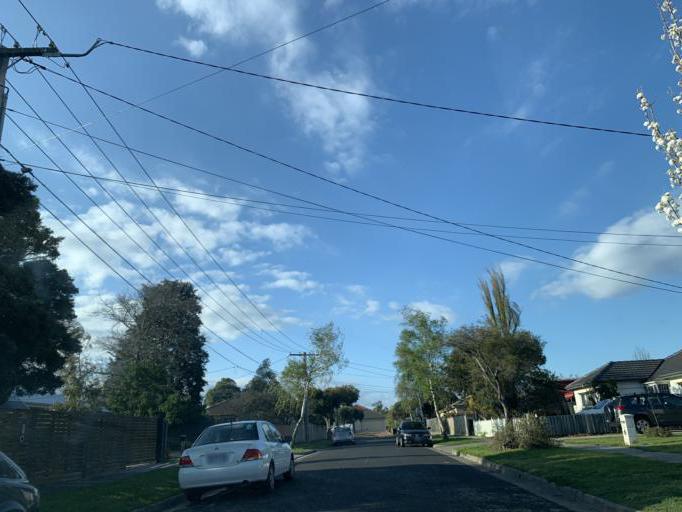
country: AU
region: Victoria
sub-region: Kingston
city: Mordialloc
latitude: -37.9884
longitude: 145.0925
